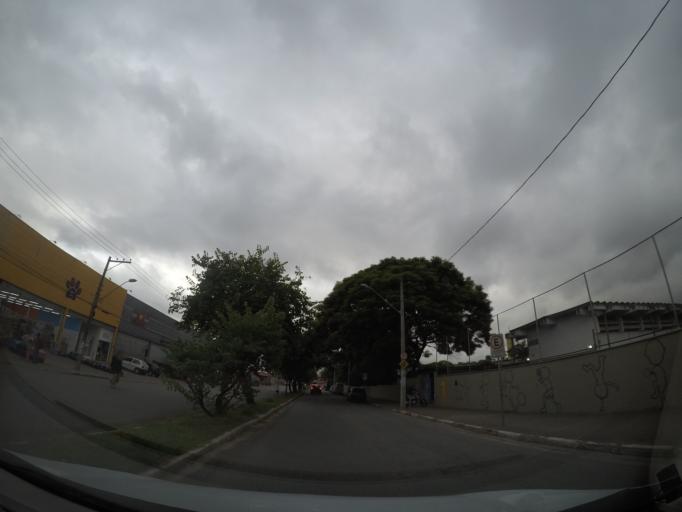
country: BR
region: Sao Paulo
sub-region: Aruja
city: Aruja
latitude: -23.4017
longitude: -46.4327
